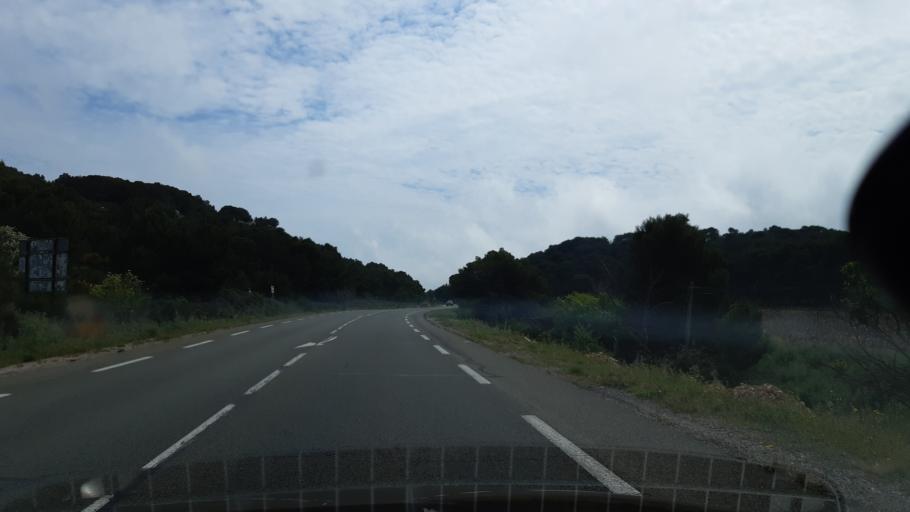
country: FR
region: Languedoc-Roussillon
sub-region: Departement de l'Aude
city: Gruissan
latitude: 43.1299
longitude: 3.0564
